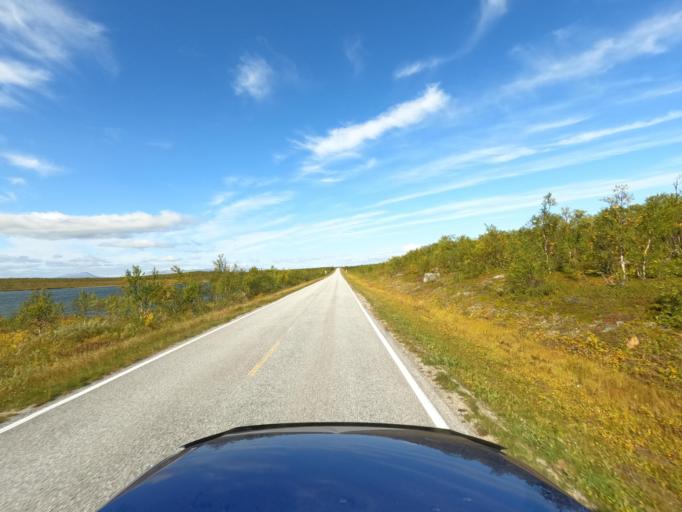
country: NO
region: Finnmark Fylke
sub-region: Karasjok
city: Karasjohka
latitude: 69.7033
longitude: 25.2522
